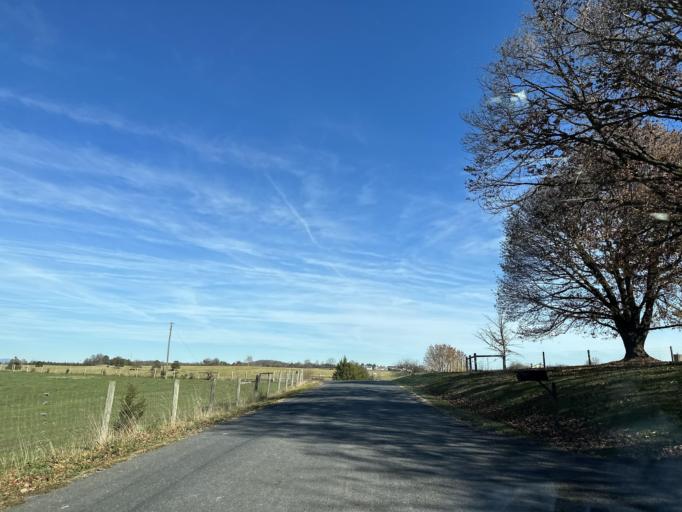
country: US
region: Virginia
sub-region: Augusta County
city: Weyers Cave
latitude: 38.2656
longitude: -78.9268
